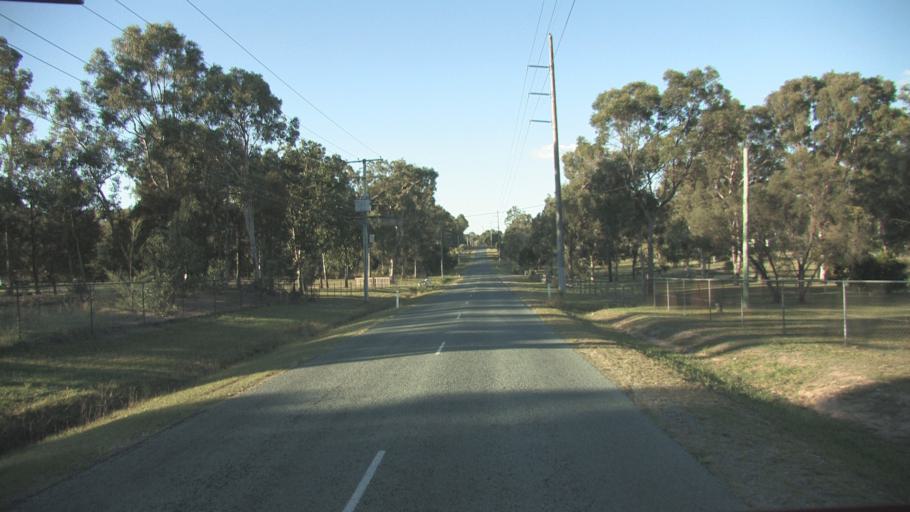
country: AU
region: Queensland
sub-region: Logan
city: Logan Reserve
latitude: -27.7326
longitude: 153.0915
